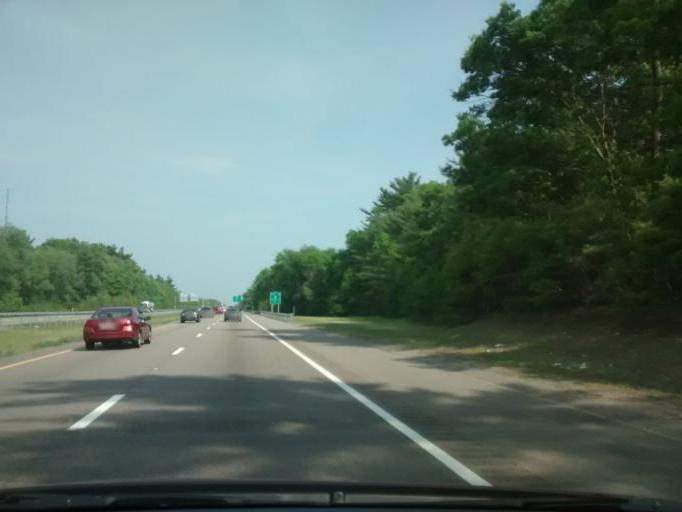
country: US
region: Massachusetts
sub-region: Plymouth County
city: Middleborough Center
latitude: 41.8942
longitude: -70.9501
